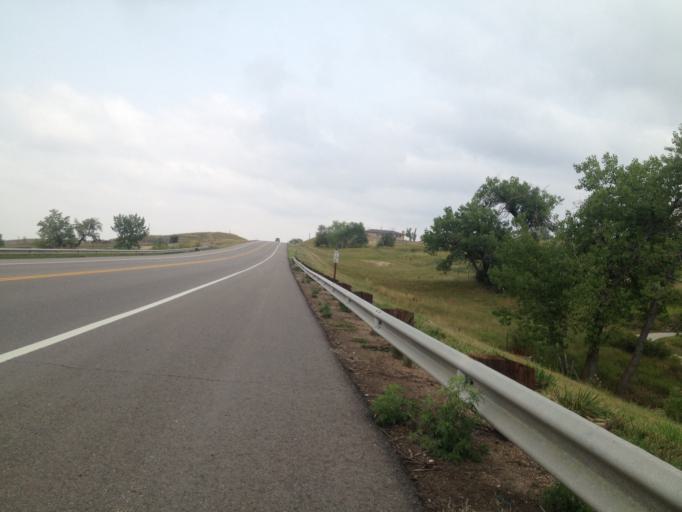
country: US
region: Colorado
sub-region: Boulder County
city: Louisville
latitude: 39.9725
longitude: -105.1219
